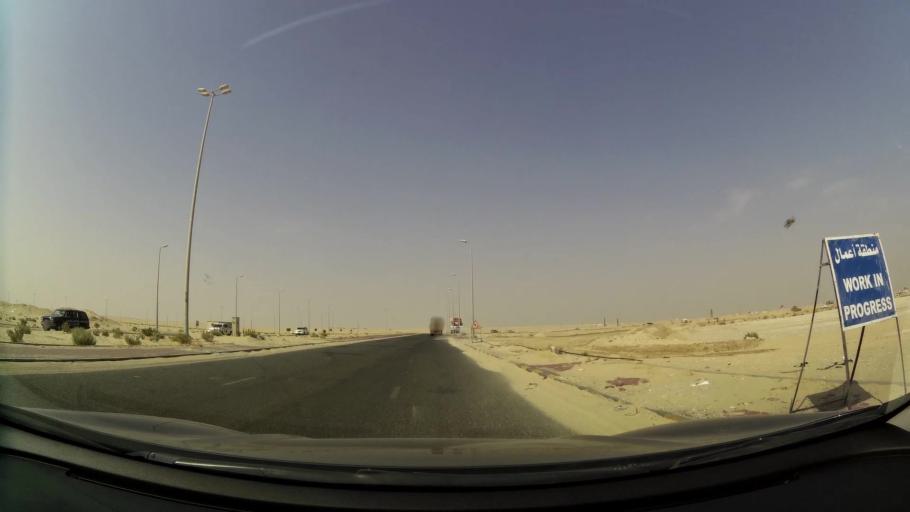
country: KW
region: Al Ahmadi
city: Al Wafrah
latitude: 28.8046
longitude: 48.0426
